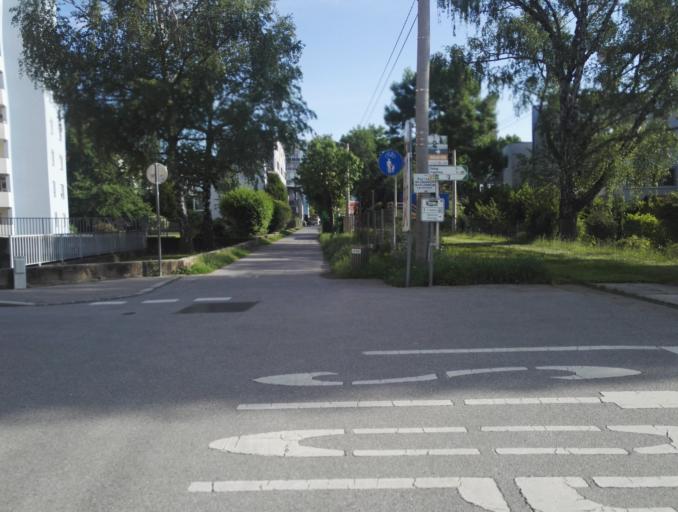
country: AT
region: Styria
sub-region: Graz Stadt
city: Goesting
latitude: 47.1008
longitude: 15.4213
